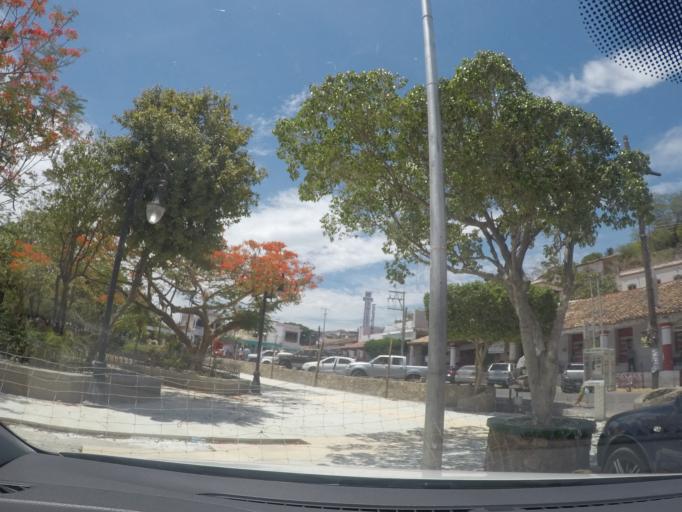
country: MX
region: Oaxaca
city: San Blas Atempa
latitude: 16.3323
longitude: -95.2318
